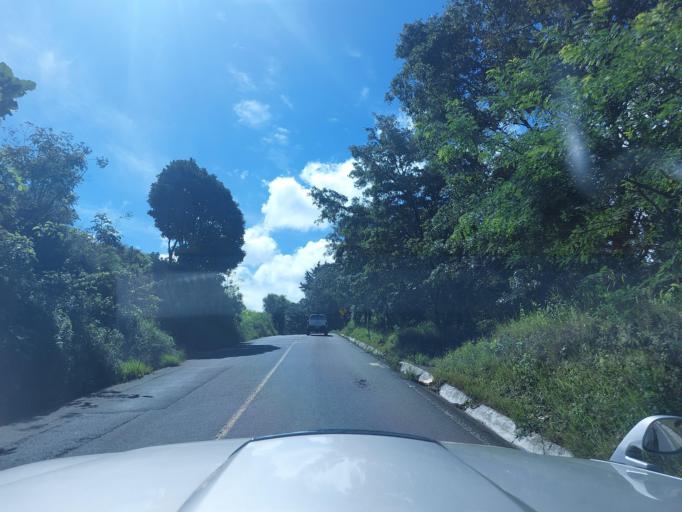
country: GT
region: Chimaltenango
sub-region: Municipio de Santa Cruz Balanya
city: Santa Cruz Balanya
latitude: 14.6994
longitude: -90.9009
